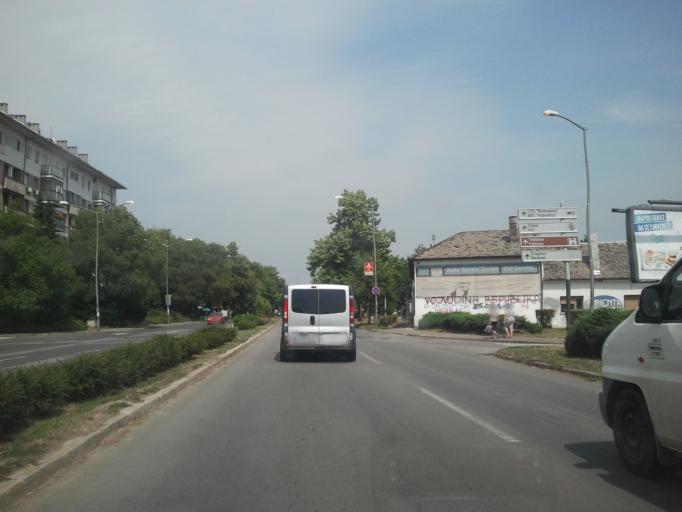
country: RS
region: Autonomna Pokrajina Vojvodina
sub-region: Juznobacki Okrug
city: Petrovaradin
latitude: 45.2489
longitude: 19.8767
